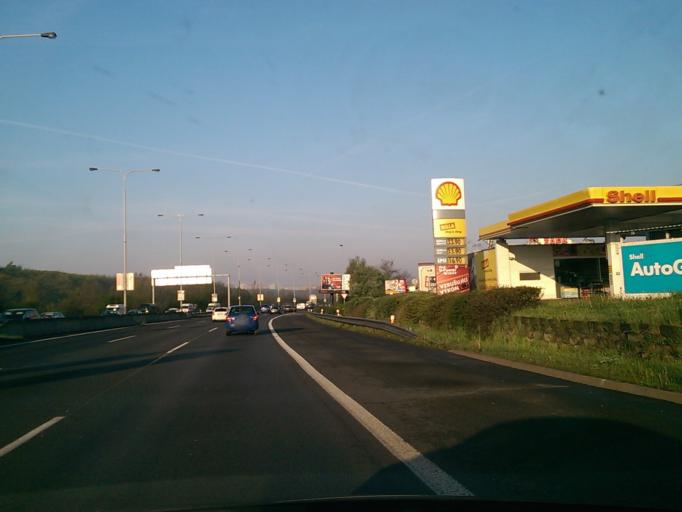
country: CZ
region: Praha
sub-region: Praha 4
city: Hodkovicky
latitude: 50.0390
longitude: 14.4676
